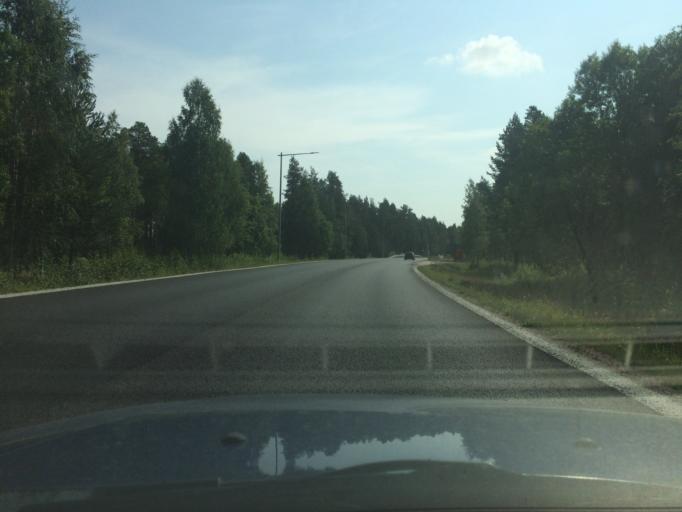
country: SE
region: Norrbotten
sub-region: Pitea Kommun
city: Pitea
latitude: 65.3299
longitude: 21.4690
